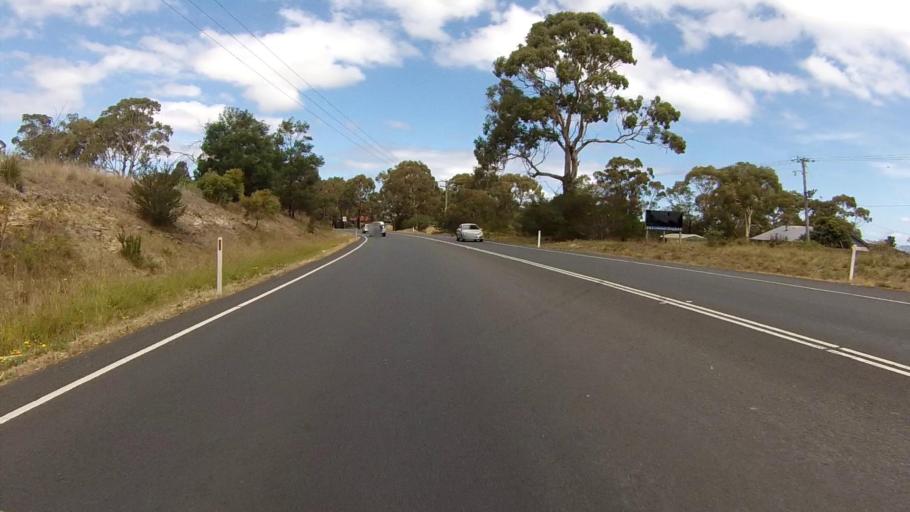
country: AU
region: Tasmania
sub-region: Sorell
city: Sorell
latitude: -42.8408
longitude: 147.6226
